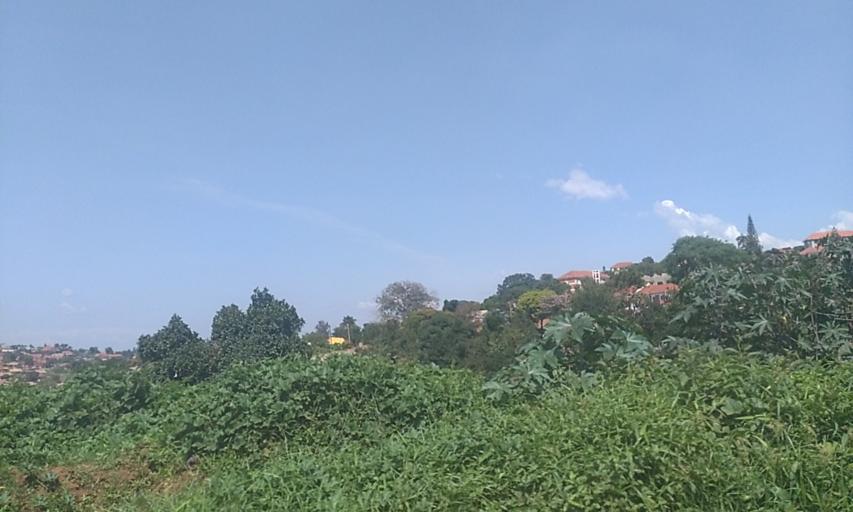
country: UG
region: Central Region
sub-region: Wakiso District
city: Kireka
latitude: 0.3609
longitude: 32.6083
